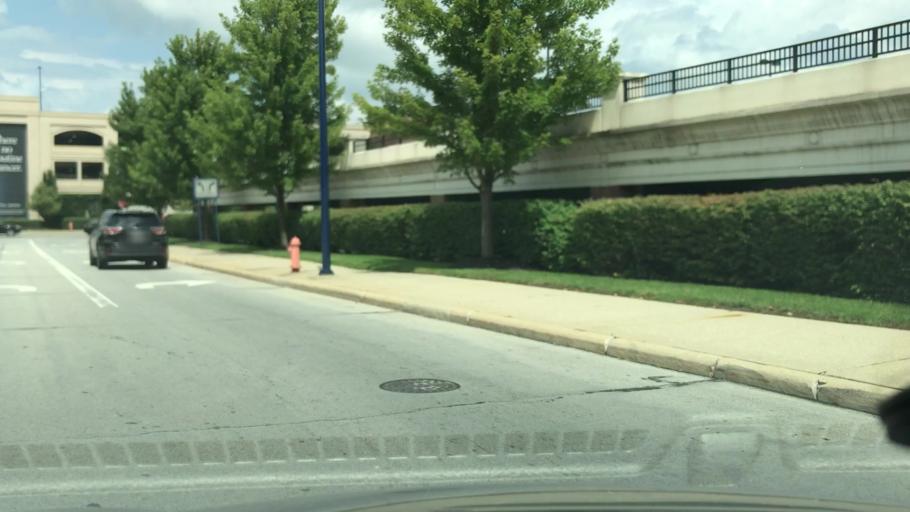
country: US
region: Ohio
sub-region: Franklin County
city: Huber Ridge
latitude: 40.0508
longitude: -82.9130
